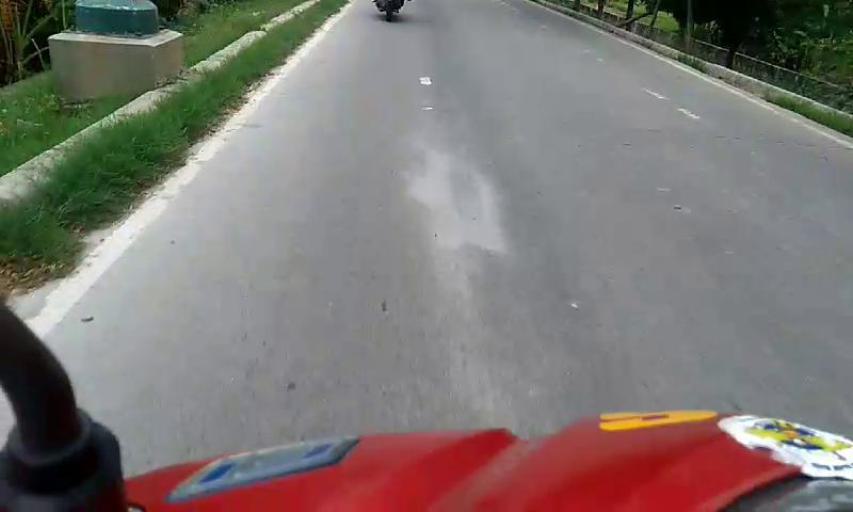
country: ID
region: West Java
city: Bekasi
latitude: -6.1407
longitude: 106.9696
